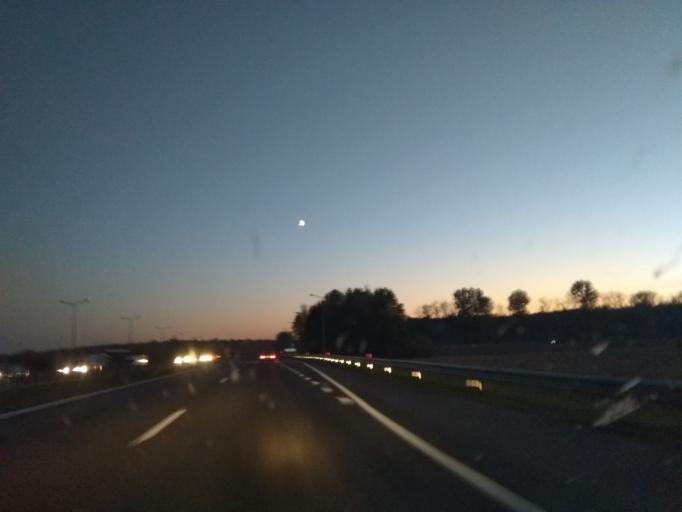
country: BY
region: Minsk
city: Enyerhyetykaw
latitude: 53.5982
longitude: 27.0433
